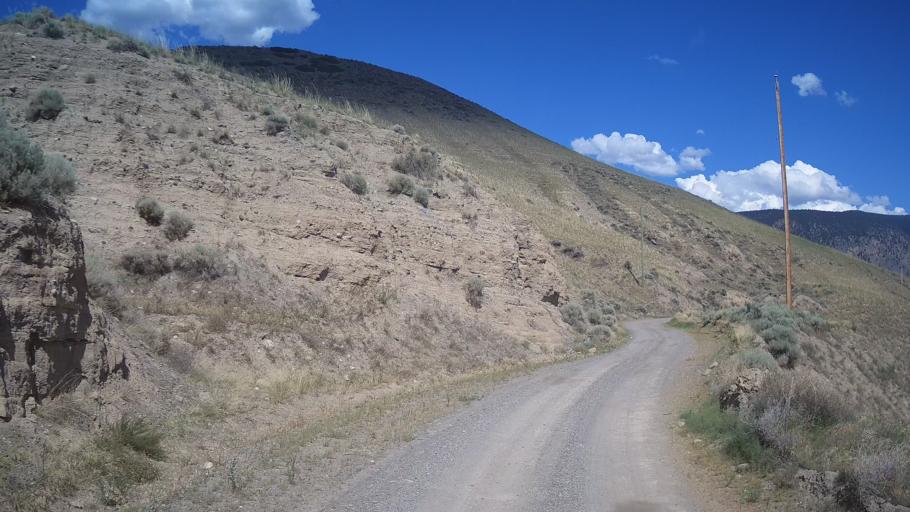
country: CA
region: British Columbia
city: Lillooet
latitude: 51.1813
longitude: -122.1233
